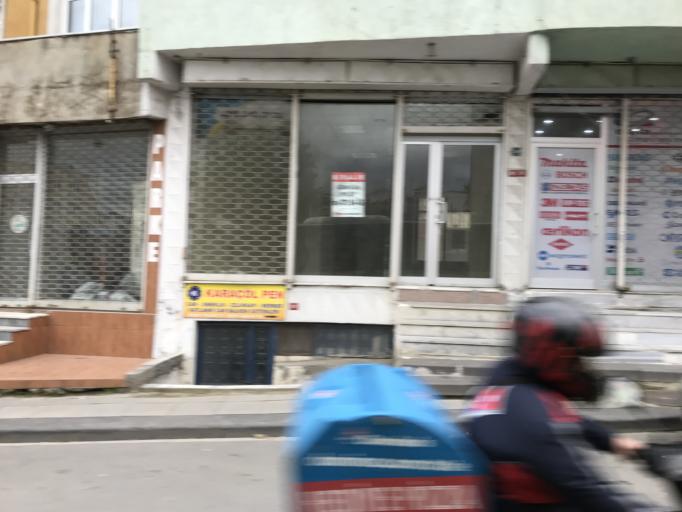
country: TR
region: Istanbul
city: Umraniye
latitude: 41.0120
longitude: 29.1681
